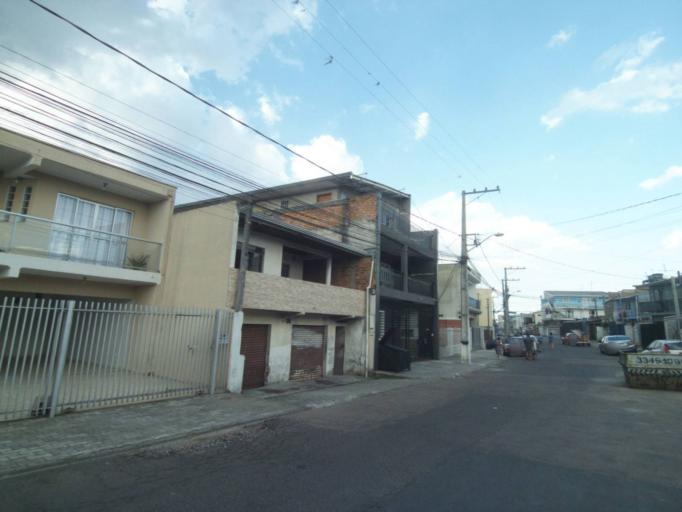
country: BR
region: Parana
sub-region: Sao Jose Dos Pinhais
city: Sao Jose dos Pinhais
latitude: -25.5341
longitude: -49.2789
